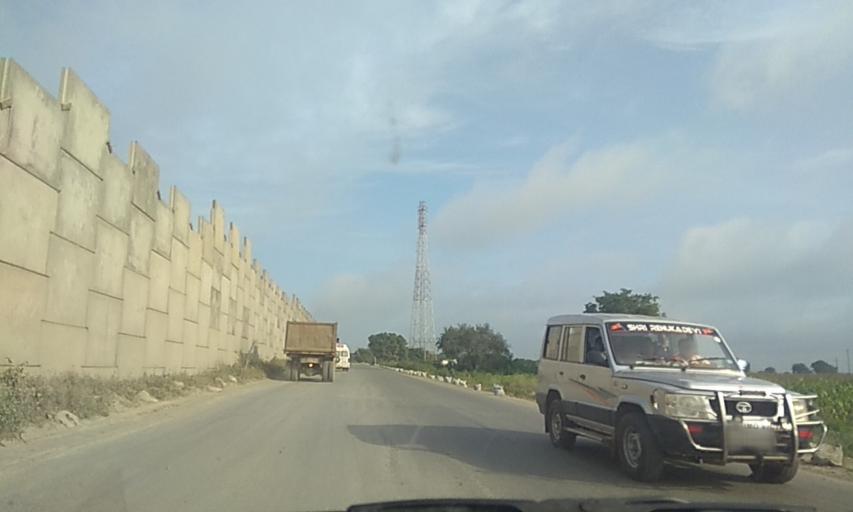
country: IN
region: Karnataka
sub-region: Haveri
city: Haveri
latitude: 14.7580
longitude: 75.4411
